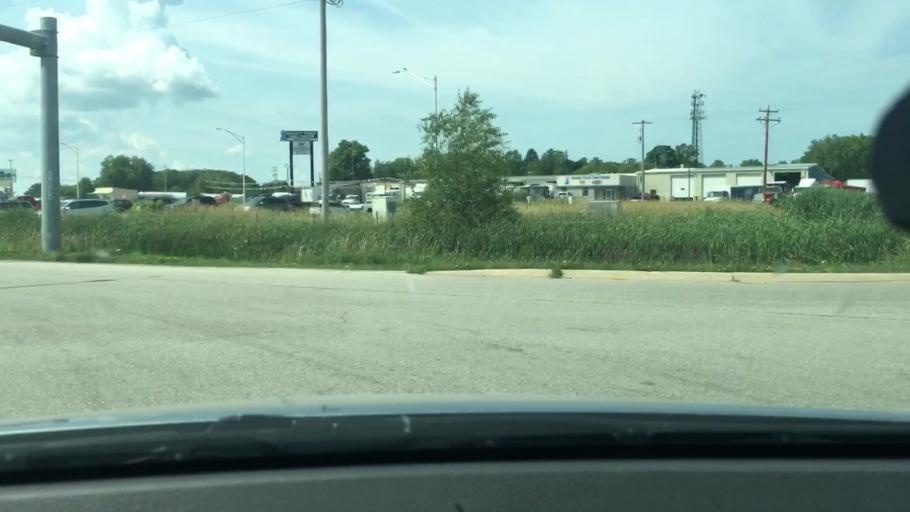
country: US
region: Wisconsin
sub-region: Winnebago County
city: Oshkosh
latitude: 44.0994
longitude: -88.5433
